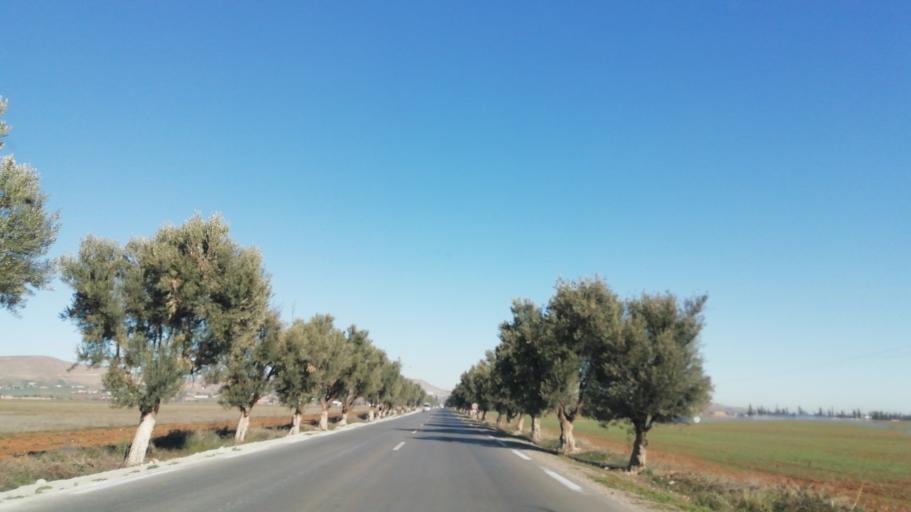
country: DZ
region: Mascara
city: Bou Hanifia el Hamamat
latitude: 35.2034
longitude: 0.1092
